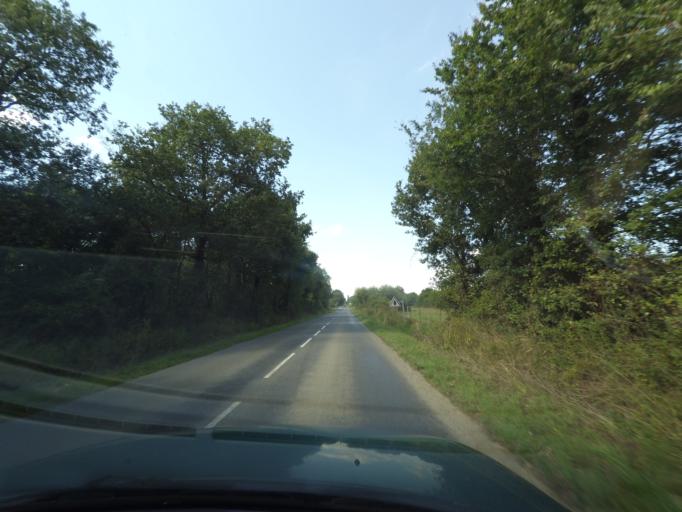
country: FR
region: Pays de la Loire
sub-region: Departement de la Loire-Atlantique
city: Saint-Lumine-de-Coutais
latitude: 47.0601
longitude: -1.7584
